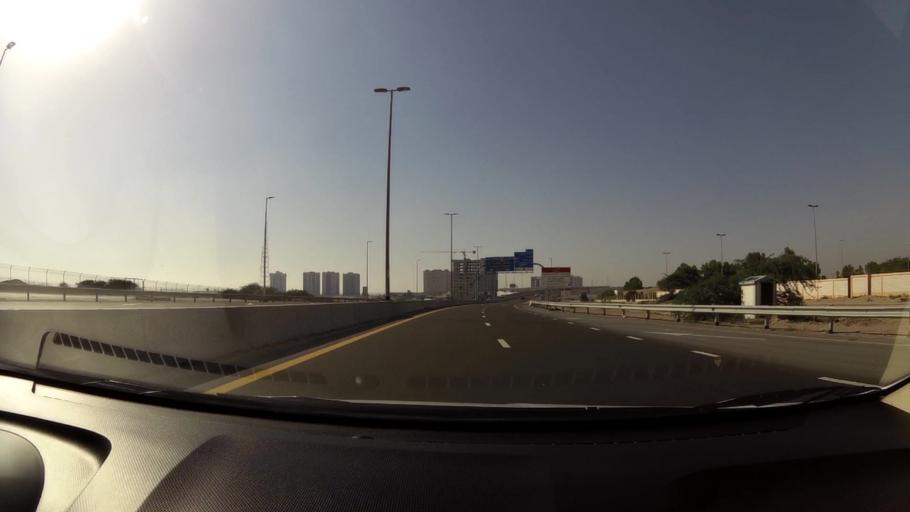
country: AE
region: Umm al Qaywayn
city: Umm al Qaywayn
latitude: 25.4882
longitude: 55.5530
